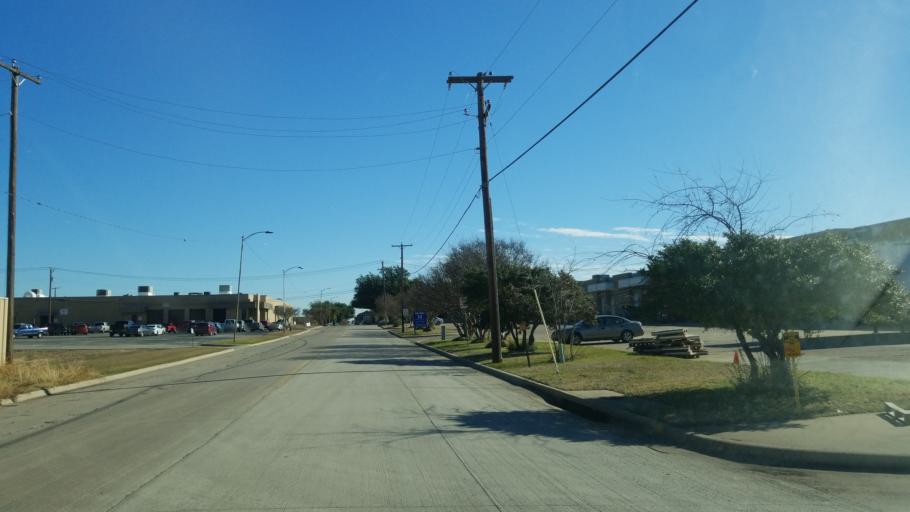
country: US
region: Texas
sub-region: Dallas County
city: Grand Prairie
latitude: 32.7447
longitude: -97.0513
